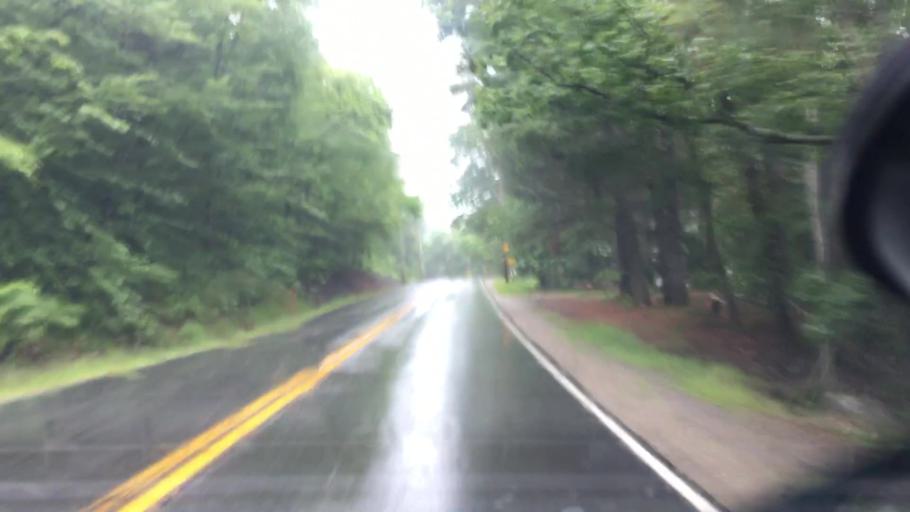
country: US
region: Maine
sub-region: Oxford County
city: Lovell
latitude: 44.2587
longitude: -70.8374
